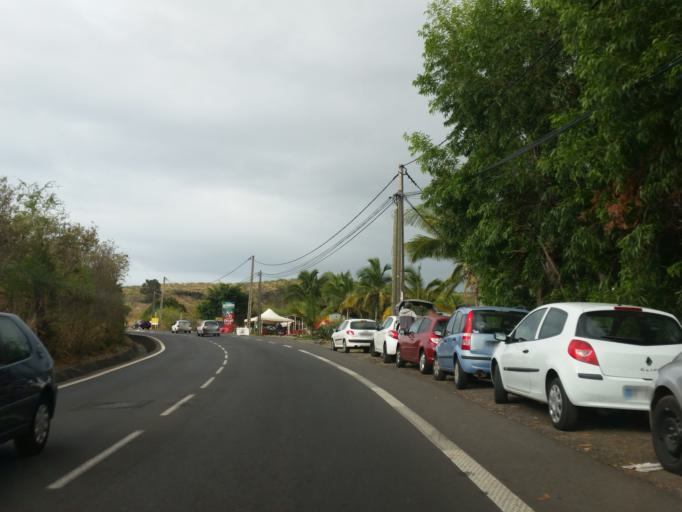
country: RE
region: Reunion
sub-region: Reunion
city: Saint-Paul
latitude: -21.0458
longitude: 55.2399
